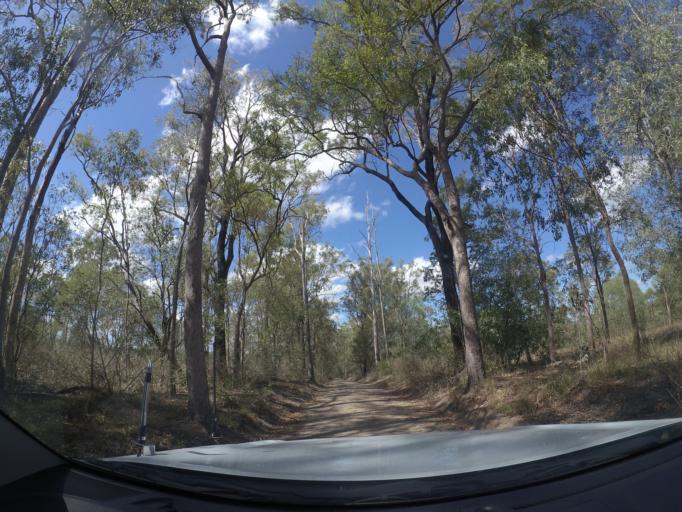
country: AU
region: Queensland
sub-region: Logan
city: Cedar Vale
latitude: -27.8393
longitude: 152.9746
